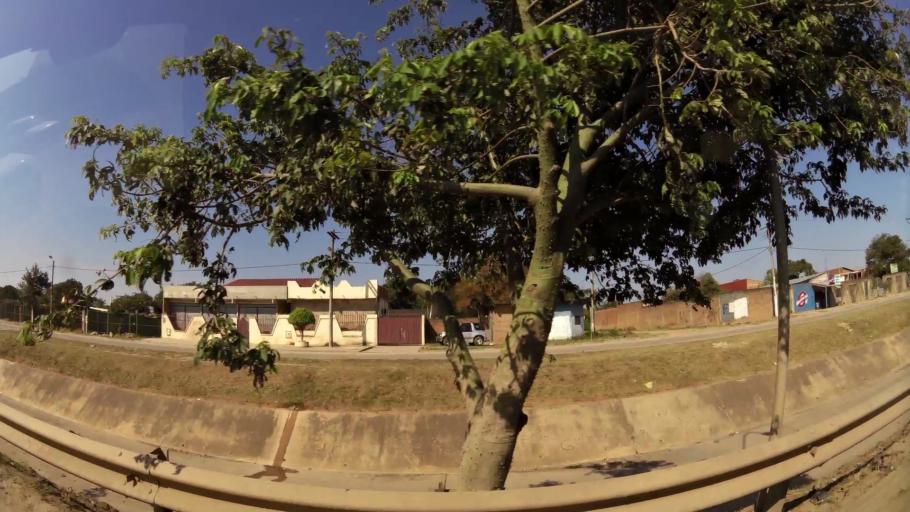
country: BO
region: Santa Cruz
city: Cotoca
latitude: -17.8037
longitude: -63.1092
